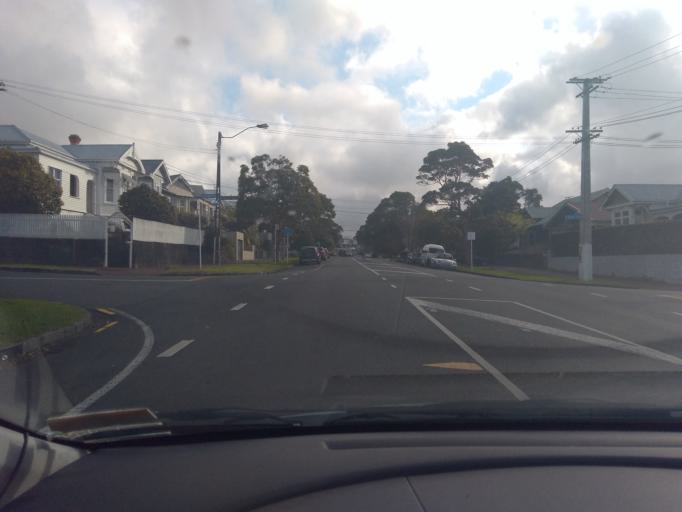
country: NZ
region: Auckland
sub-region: Auckland
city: Auckland
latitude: -36.8627
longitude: 174.7414
